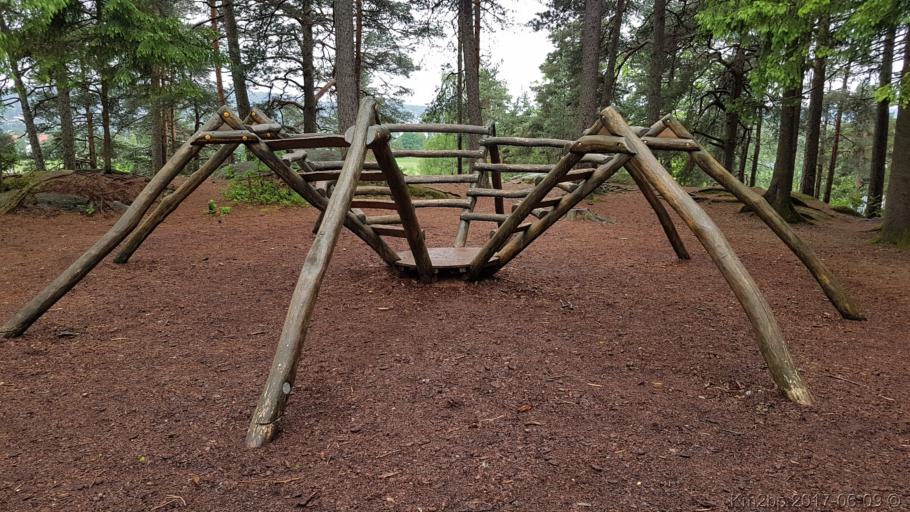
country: NO
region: Akershus
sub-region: Skedsmo
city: Lillestrom
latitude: 59.9575
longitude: 11.0692
